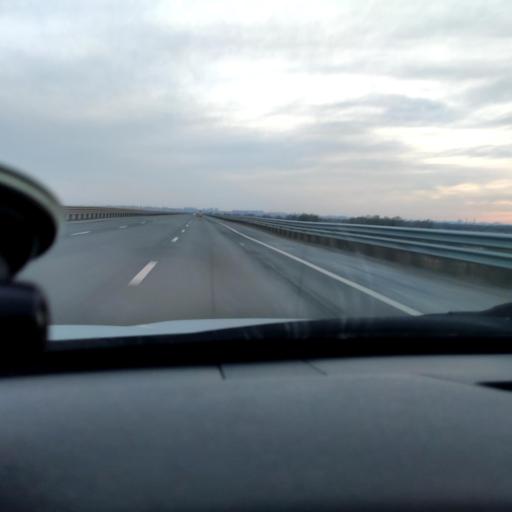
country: RU
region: Samara
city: Smyshlyayevka
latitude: 53.1549
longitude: 50.3450
